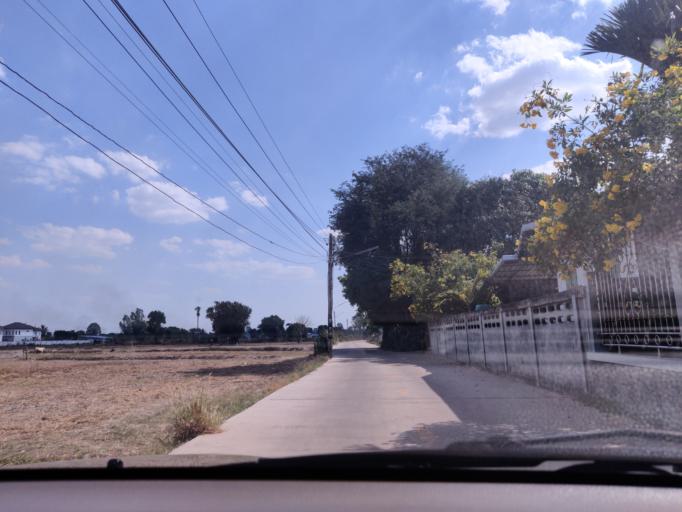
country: TH
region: Sisaket
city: Si Sa Ket
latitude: 15.1025
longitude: 104.3551
